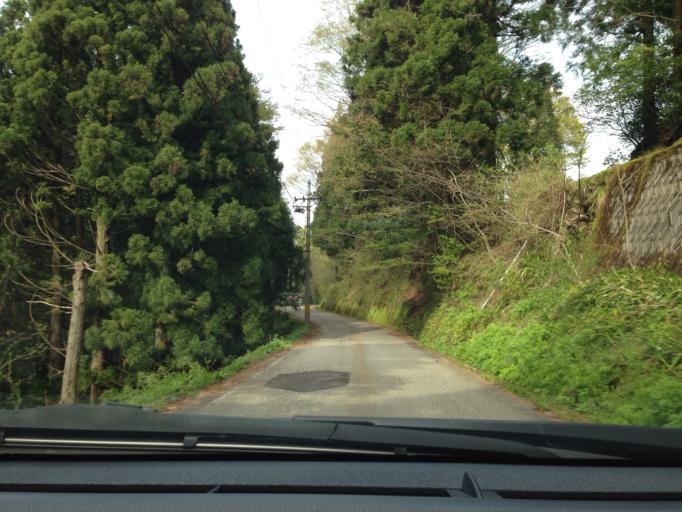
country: JP
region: Toyama
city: Fukumitsu
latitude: 36.4894
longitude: 136.8228
